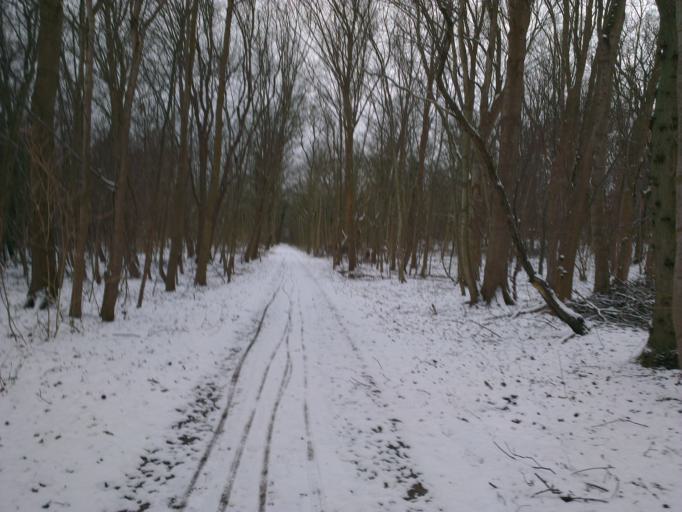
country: DK
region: Capital Region
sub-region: Frederikssund Kommune
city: Jaegerspris
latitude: 55.8530
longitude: 11.9617
